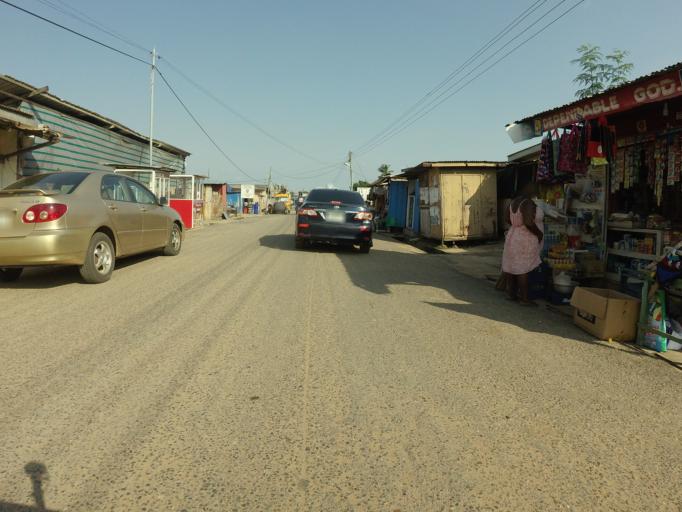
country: GH
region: Greater Accra
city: Dome
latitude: 5.6133
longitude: -0.2350
